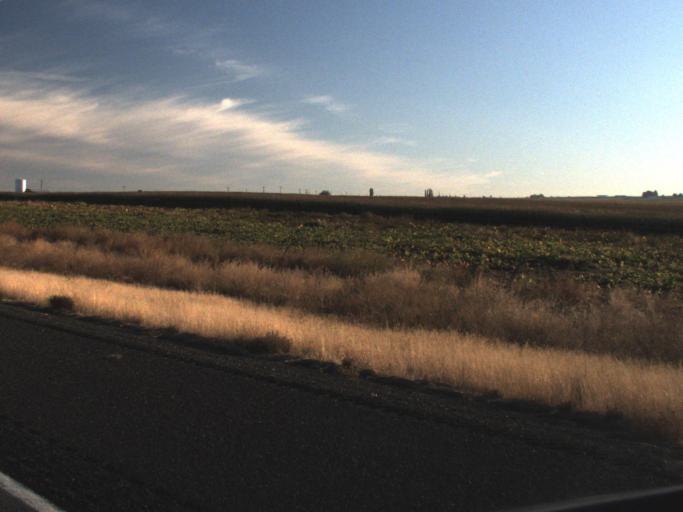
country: US
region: Washington
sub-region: Franklin County
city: Pasco
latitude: 46.3537
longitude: -119.0876
